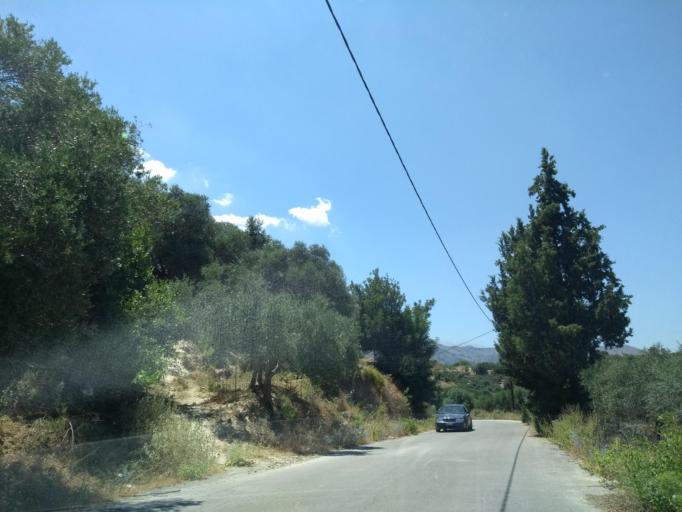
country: GR
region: Crete
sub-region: Nomos Chanias
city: Georgioupolis
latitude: 35.3184
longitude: 24.3155
